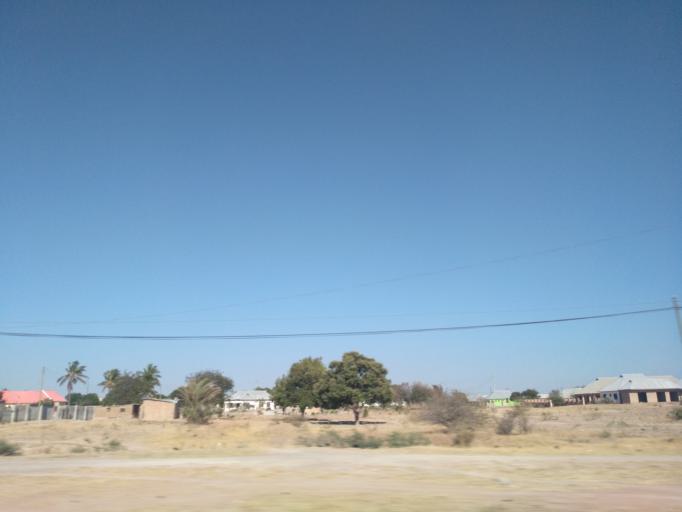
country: TZ
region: Dodoma
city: Dodoma
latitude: -6.1158
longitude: 35.7475
